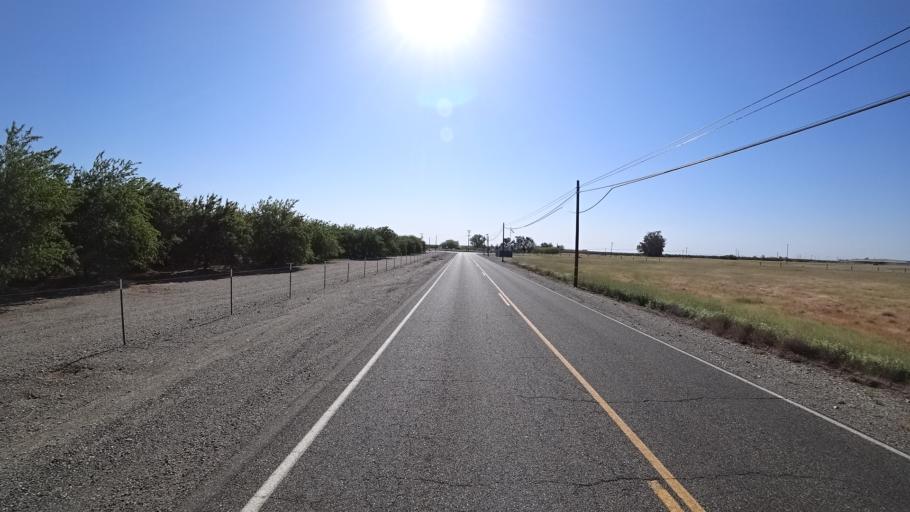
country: US
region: California
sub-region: Glenn County
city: Orland
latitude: 39.7259
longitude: -122.1428
